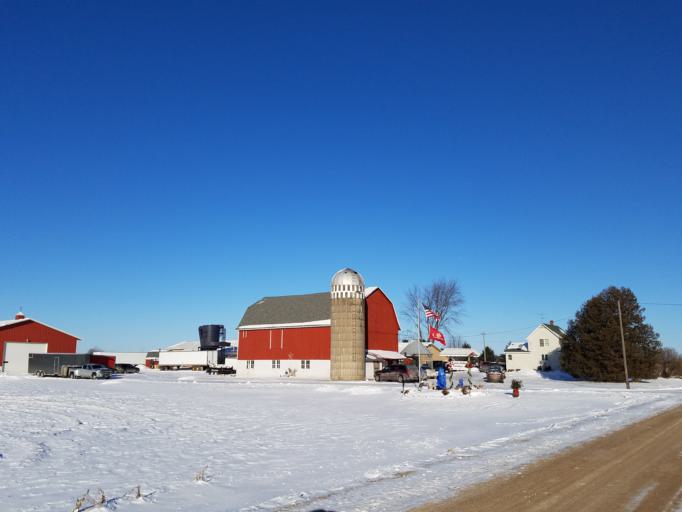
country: US
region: Wisconsin
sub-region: Clark County
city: Loyal
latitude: 44.6664
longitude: -90.4173
